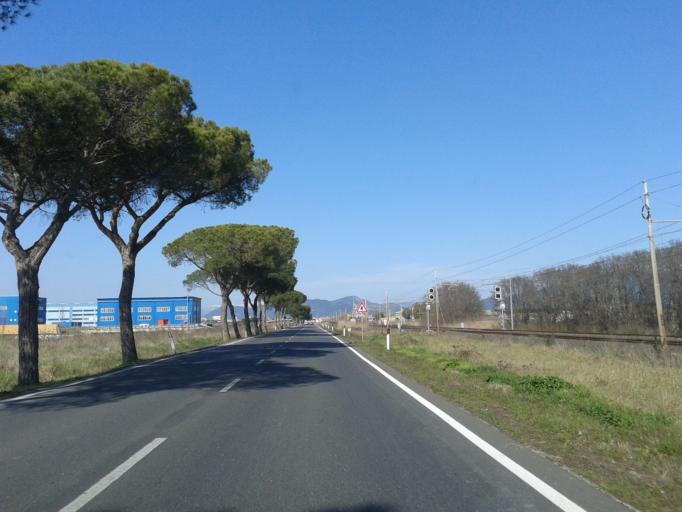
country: IT
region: Tuscany
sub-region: Province of Pisa
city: Pisa
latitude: 43.6835
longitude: 10.3814
